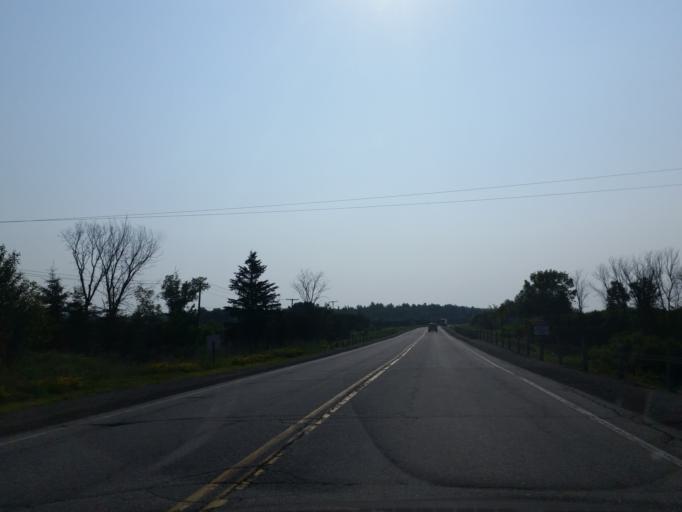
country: CA
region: Ontario
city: Greater Sudbury
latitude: 46.4304
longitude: -80.2288
